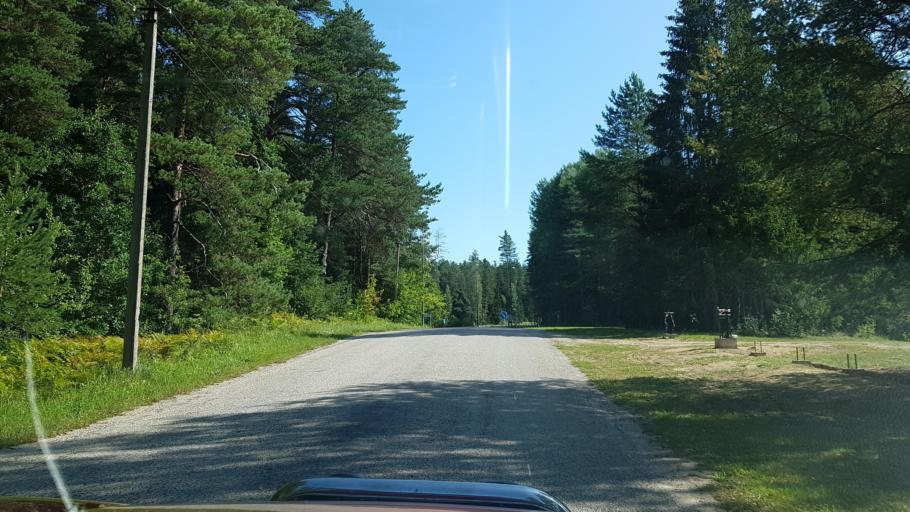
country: EE
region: Vorumaa
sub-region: Voru linn
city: Voru
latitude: 57.7376
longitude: 27.2759
